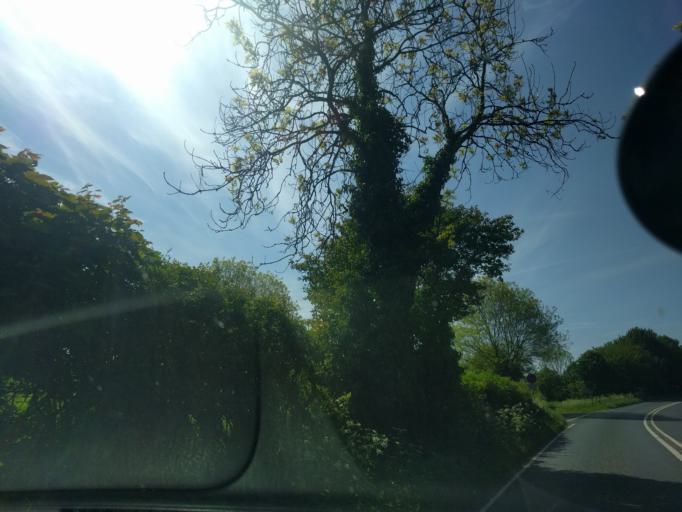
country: GB
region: England
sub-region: Somerset
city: Evercreech
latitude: 51.1369
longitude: -2.5510
